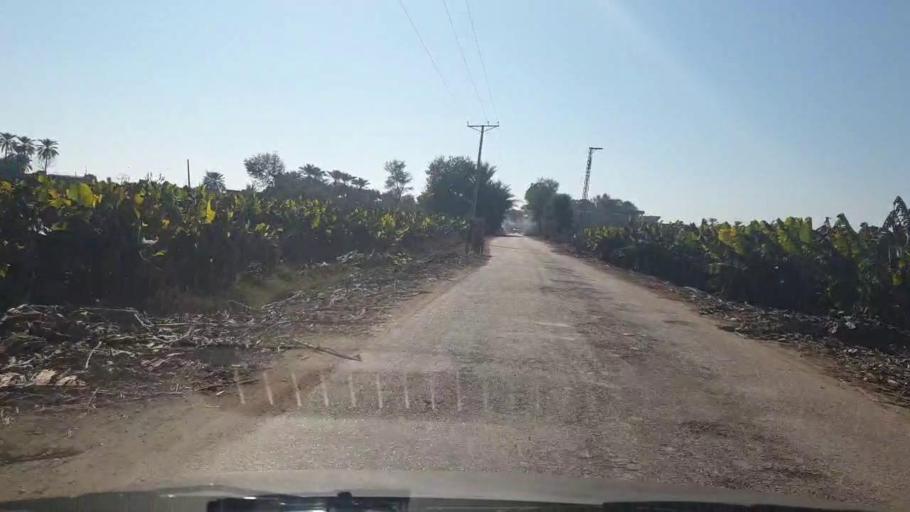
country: PK
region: Sindh
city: Bozdar
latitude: 27.2476
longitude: 68.6520
